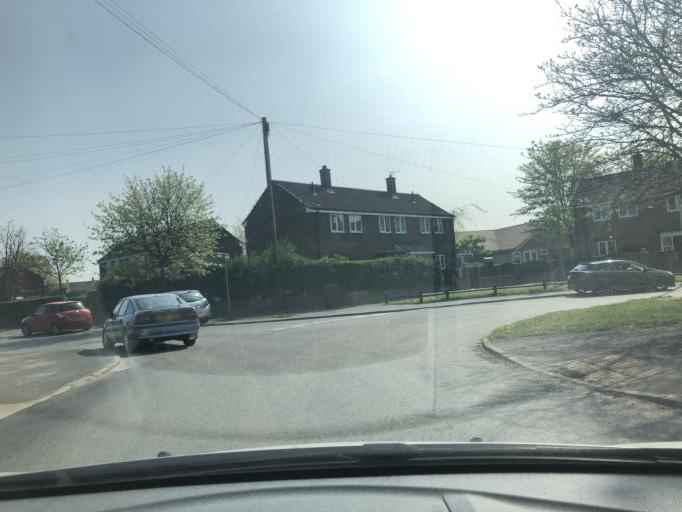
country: GB
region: England
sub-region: Borough of Stockport
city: Bredbury
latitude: 53.4321
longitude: -2.1353
